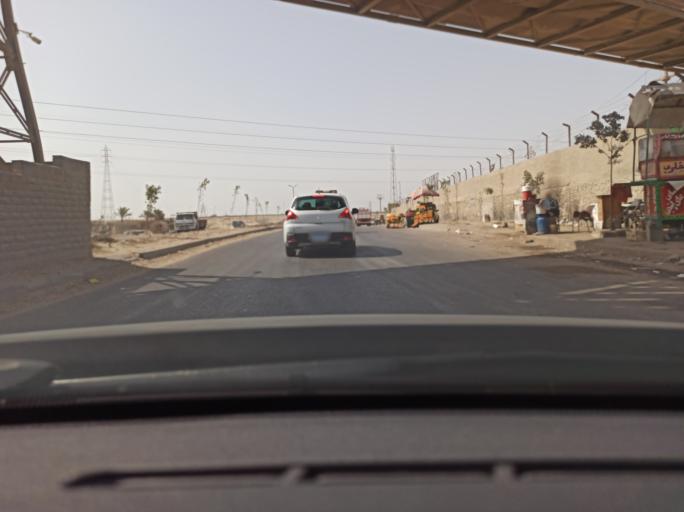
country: EG
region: Muhafazat al Qahirah
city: Halwan
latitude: 29.7923
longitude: 31.3482
